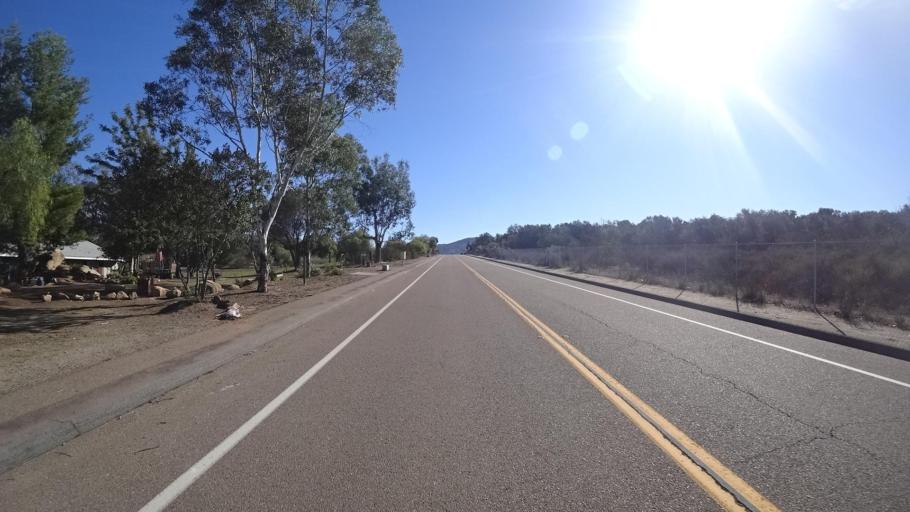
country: US
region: California
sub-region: San Diego County
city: Jamul
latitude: 32.7221
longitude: -116.8662
